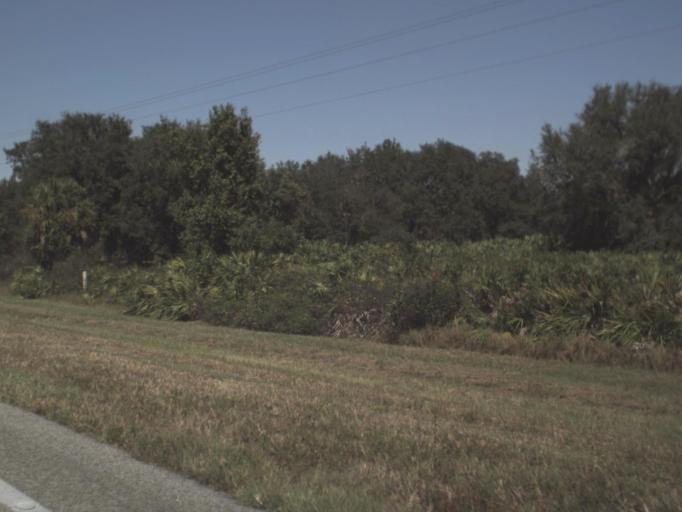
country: US
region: Florida
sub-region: Hendry County
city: Port LaBelle
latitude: 26.9908
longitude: -81.3254
